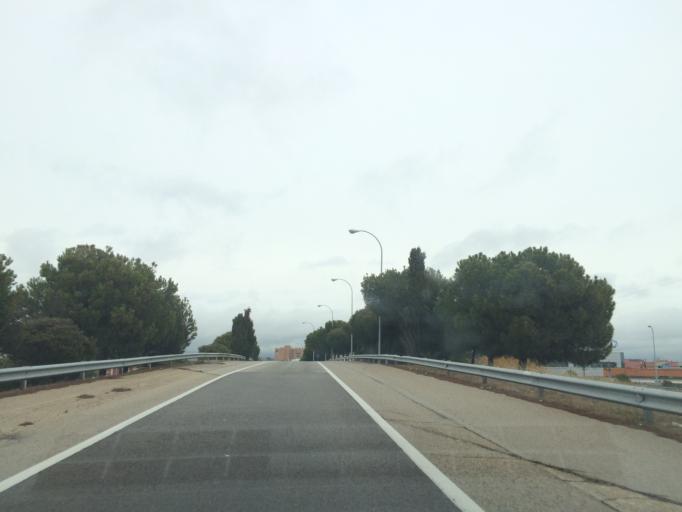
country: ES
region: Madrid
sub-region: Provincia de Madrid
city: Tres Cantos
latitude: 40.6012
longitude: -3.7196
